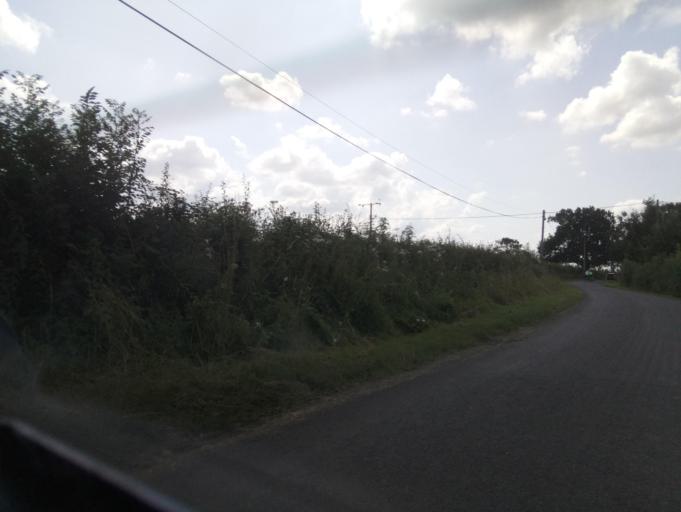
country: GB
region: England
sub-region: Wiltshire
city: Charlton
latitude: 51.5666
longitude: -2.0361
